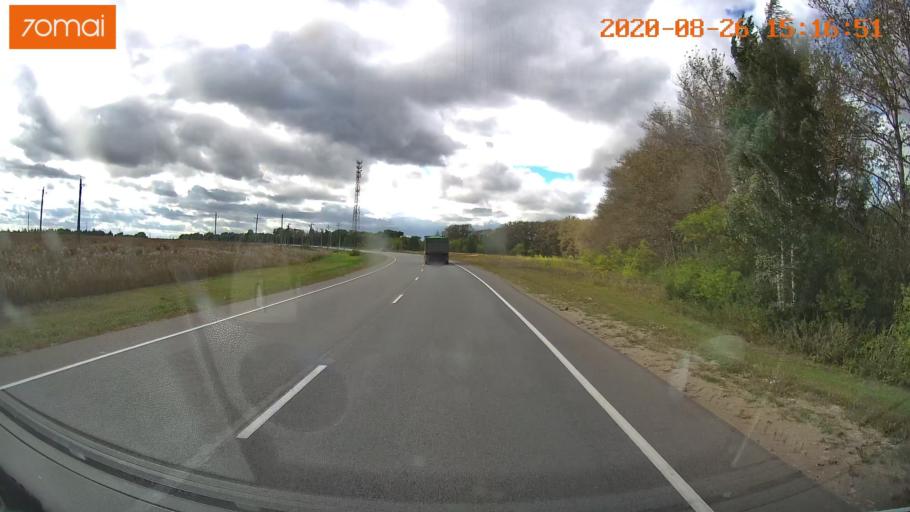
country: RU
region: Tula
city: Kimovsk
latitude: 54.1473
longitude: 38.5623
